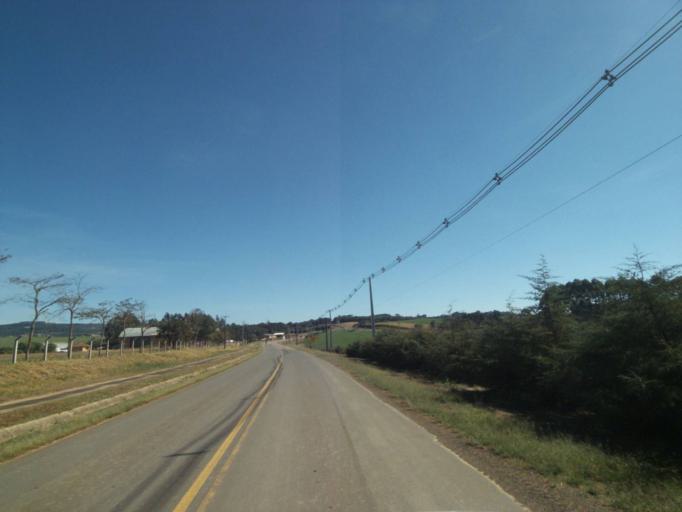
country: BR
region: Parana
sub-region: Tibagi
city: Tibagi
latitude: -24.5261
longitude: -50.4392
